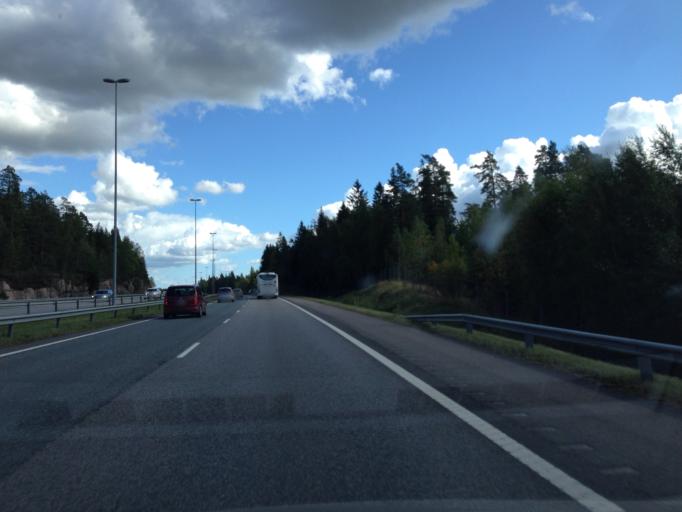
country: FI
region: Uusimaa
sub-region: Helsinki
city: Kirkkonummi
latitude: 60.2688
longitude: 24.4696
